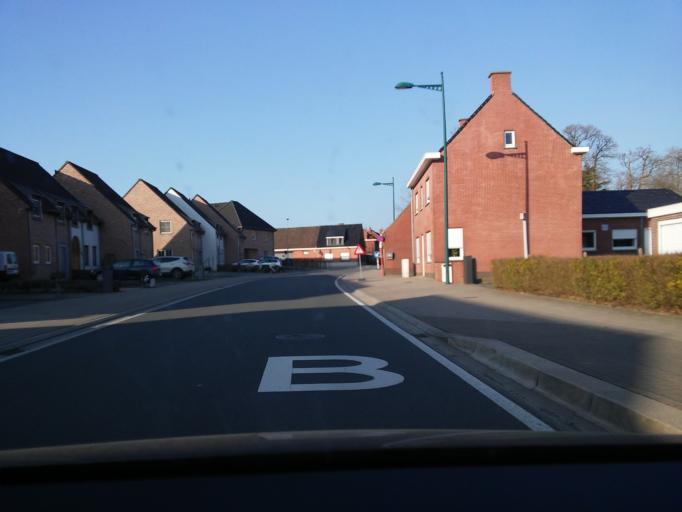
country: BE
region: Flanders
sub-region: Provincie Oost-Vlaanderen
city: Aalter
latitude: 51.0444
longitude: 3.4649
